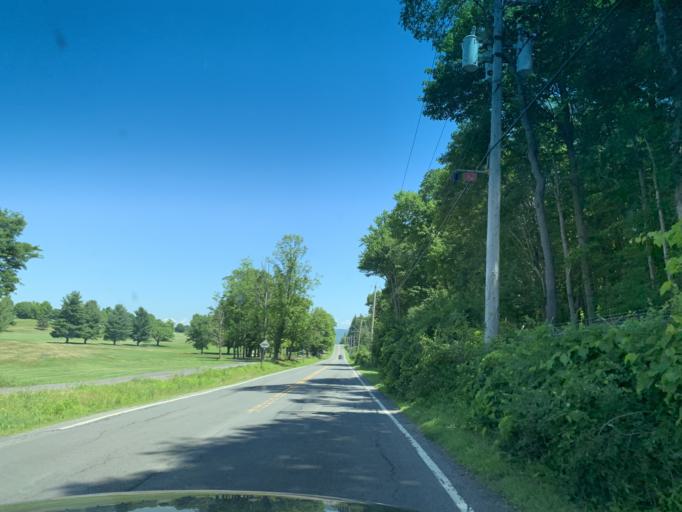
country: US
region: New York
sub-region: Oneida County
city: Utica
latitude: 43.0725
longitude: -75.2389
